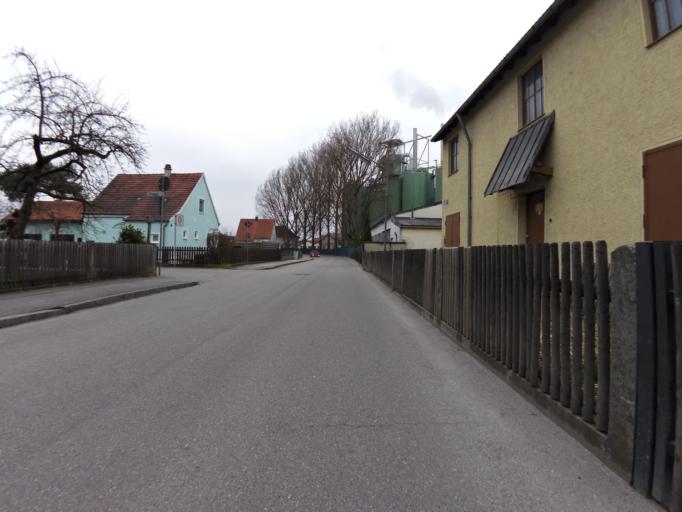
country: DE
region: Bavaria
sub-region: Upper Bavaria
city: Moosburg
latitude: 48.4704
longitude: 11.9443
